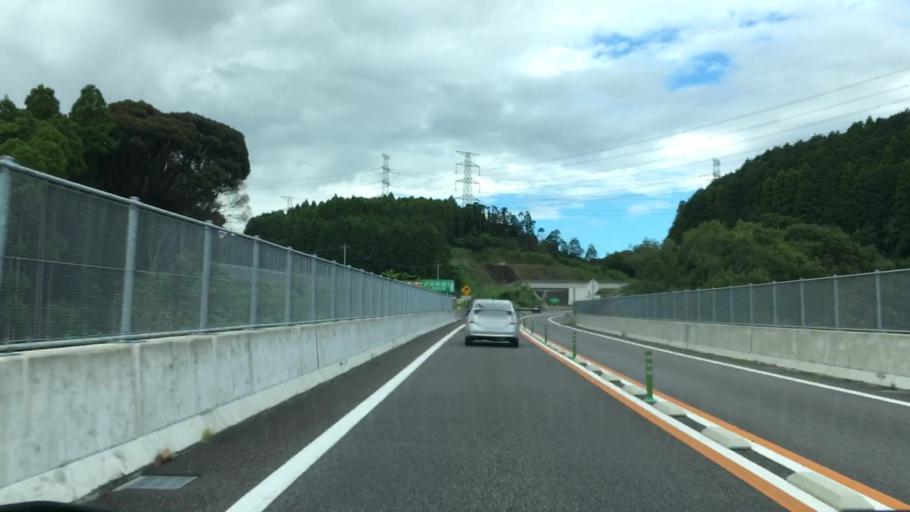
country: JP
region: Saga Prefecture
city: Imaricho-ko
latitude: 33.3491
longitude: 129.9245
